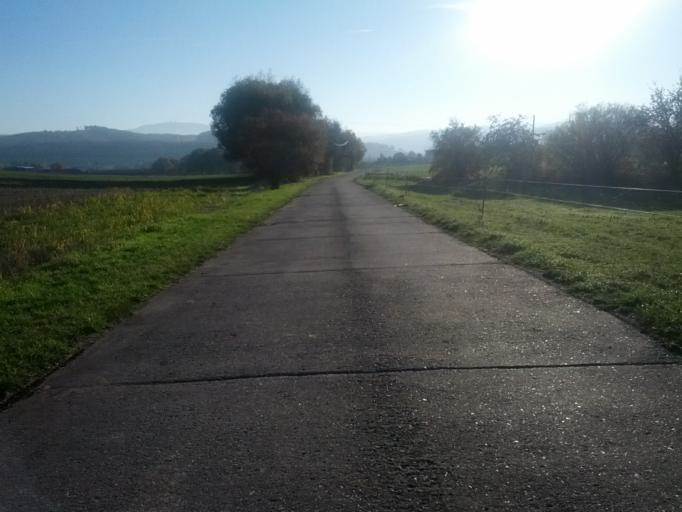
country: DE
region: Thuringia
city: Mechterstadt
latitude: 50.9516
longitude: 10.5006
